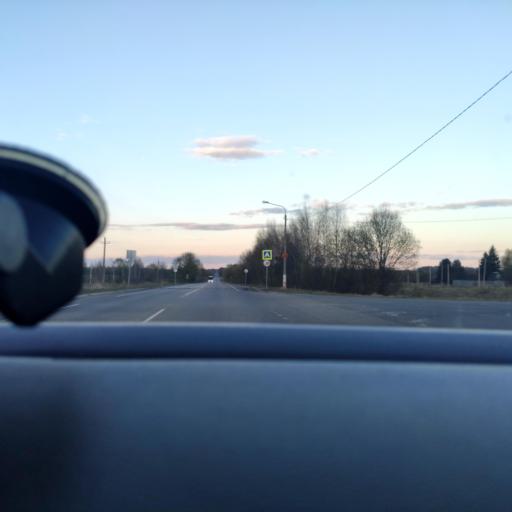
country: RU
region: Moskovskaya
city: Krasnyy Tkach
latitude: 55.4285
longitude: 39.2142
